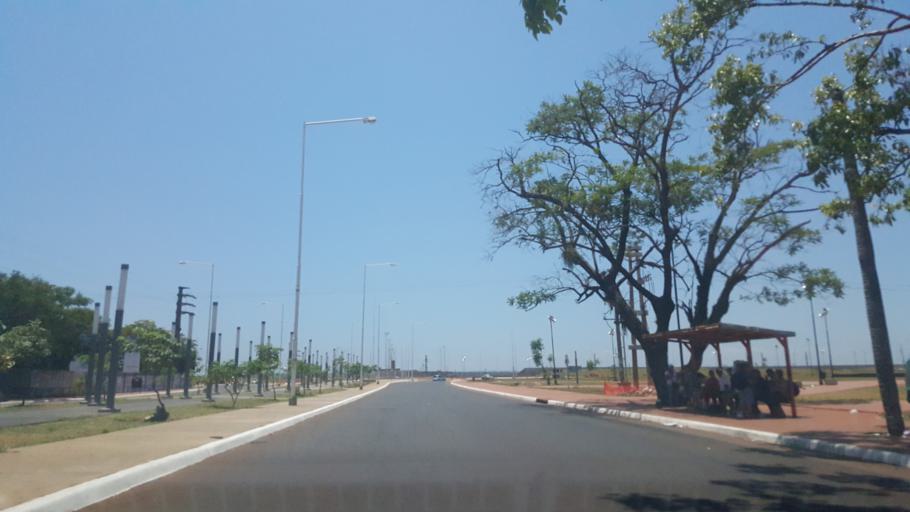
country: AR
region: Misiones
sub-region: Departamento de Capital
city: Posadas
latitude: -27.3755
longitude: -55.8879
